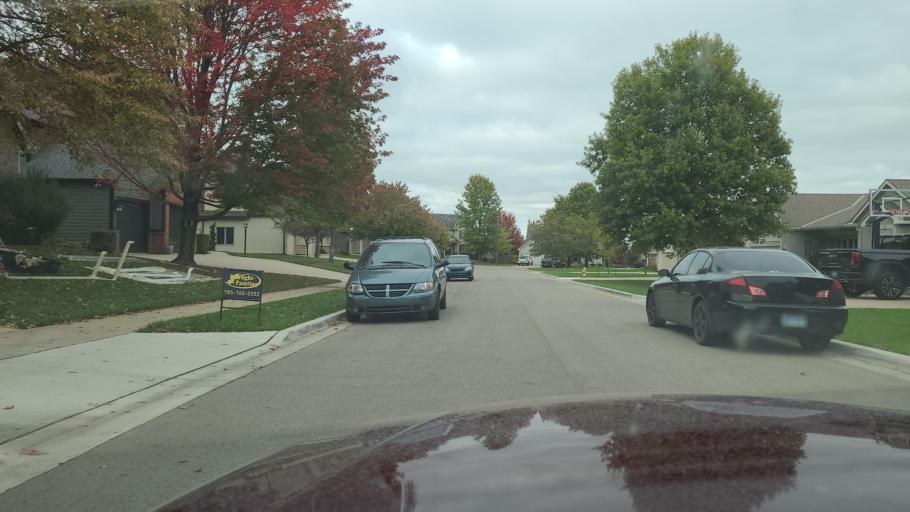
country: US
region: Kansas
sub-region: Douglas County
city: Lawrence
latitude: 38.9698
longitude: -95.3145
